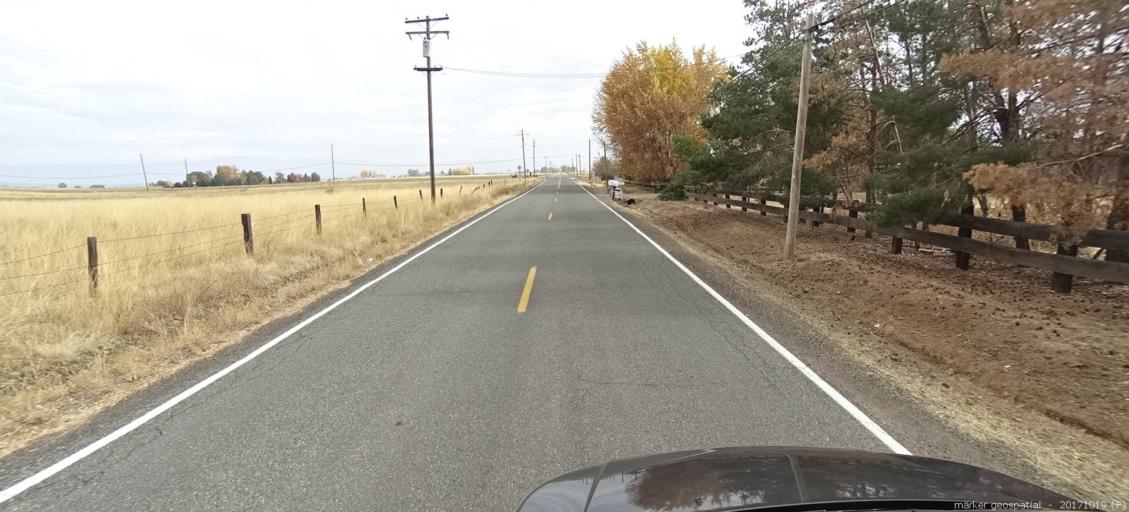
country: US
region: California
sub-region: Shasta County
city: Burney
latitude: 41.0616
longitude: -121.5112
